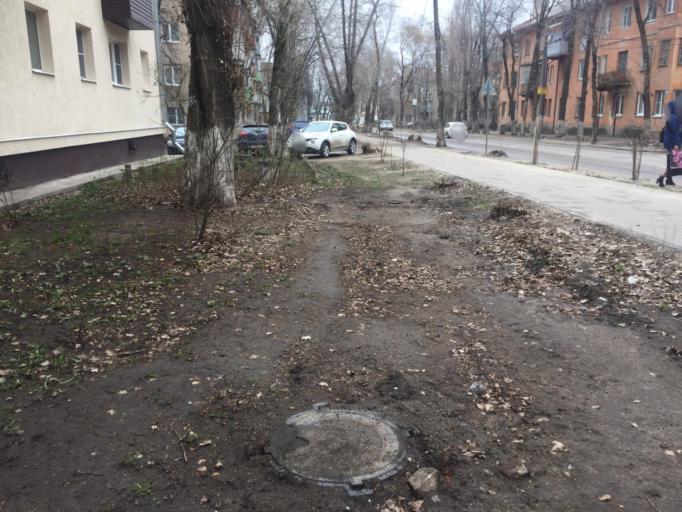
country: RU
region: Voronezj
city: Voronezh
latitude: 51.6777
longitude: 39.1535
